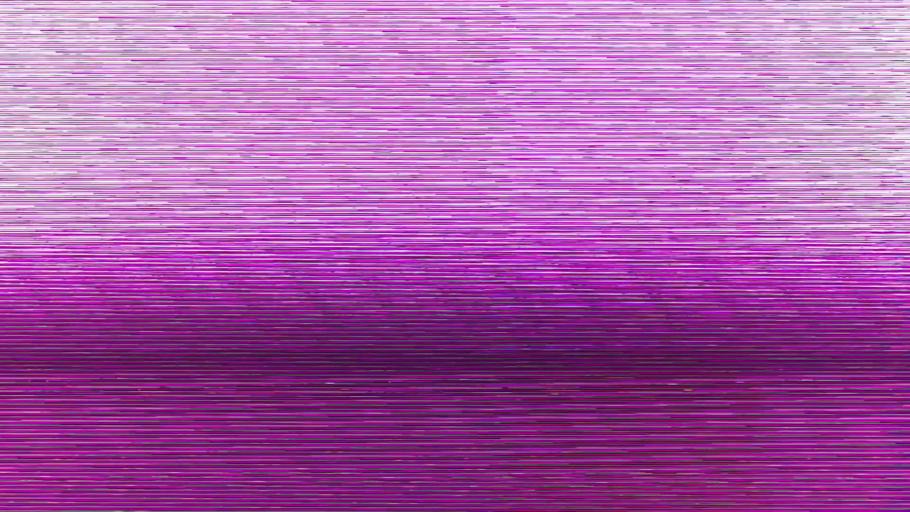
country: US
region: Michigan
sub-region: Wayne County
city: Garden City
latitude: 42.3408
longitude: -83.3496
